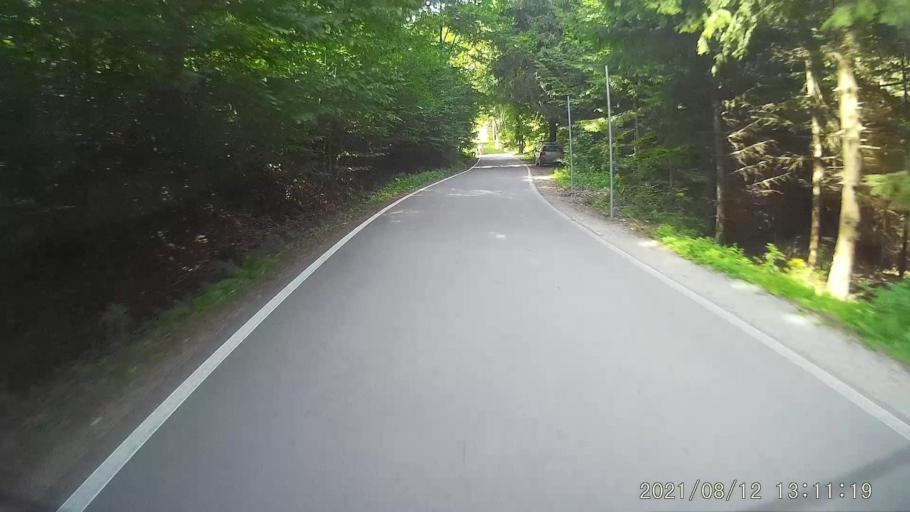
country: PL
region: Lower Silesian Voivodeship
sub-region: Powiat klodzki
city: Stronie Slaskie
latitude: 50.2435
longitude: 16.8504
